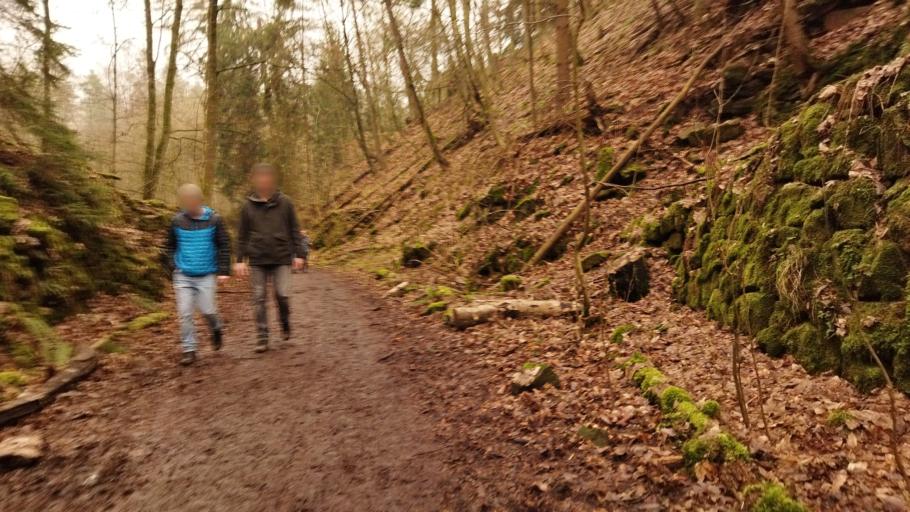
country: DE
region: Baden-Wuerttemberg
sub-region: Regierungsbezirk Stuttgart
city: Weinsberg
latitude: 49.1364
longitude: 9.2664
